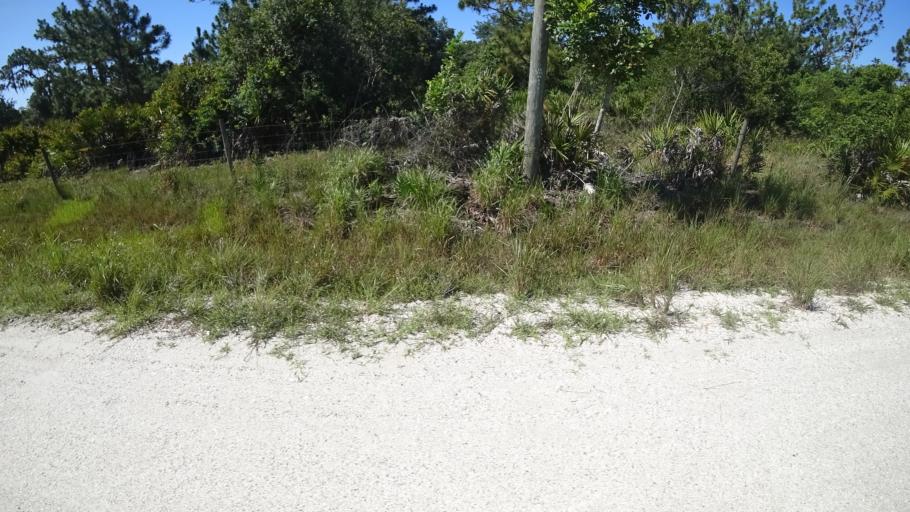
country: US
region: Florida
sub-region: Sarasota County
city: The Meadows
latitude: 27.4090
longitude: -82.2967
